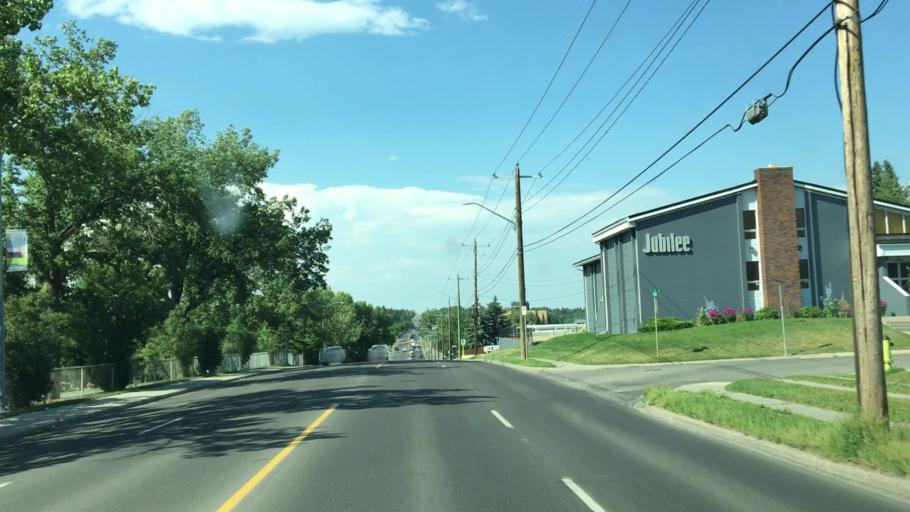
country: CA
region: Alberta
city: Calgary
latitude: 51.0839
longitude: -114.0715
